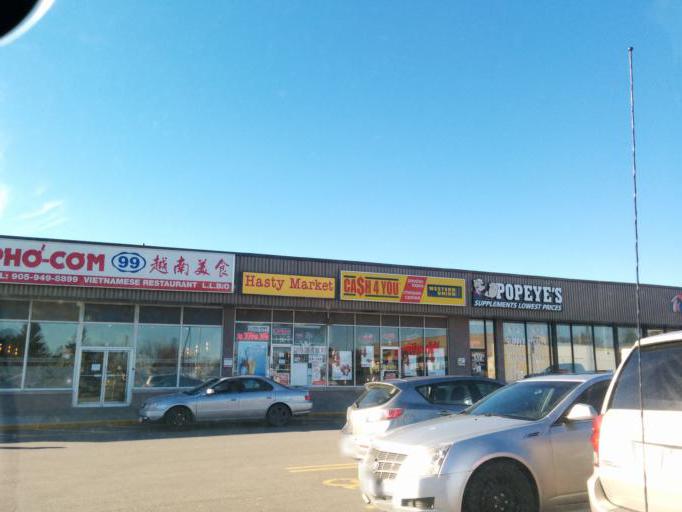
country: CA
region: Ontario
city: Etobicoke
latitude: 43.6103
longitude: -79.5869
